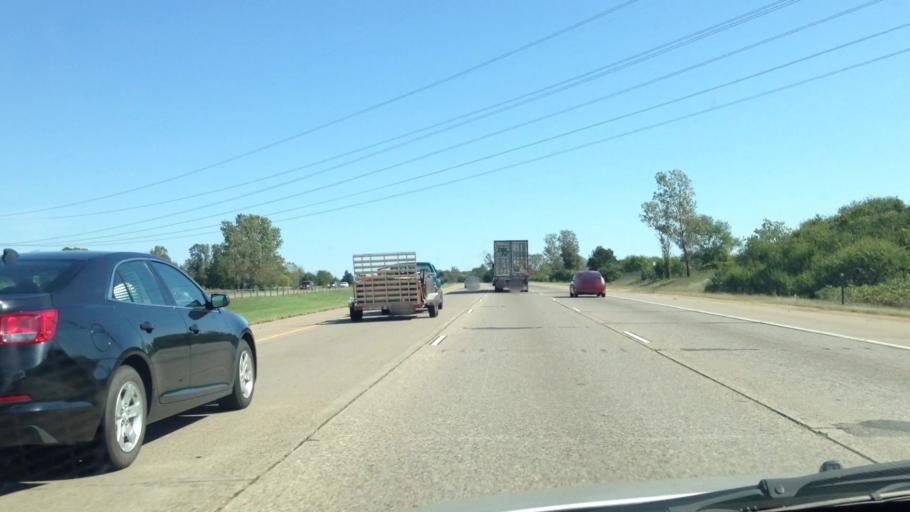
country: US
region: Minnesota
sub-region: Washington County
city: Lakeland
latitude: 44.9487
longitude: -92.8194
